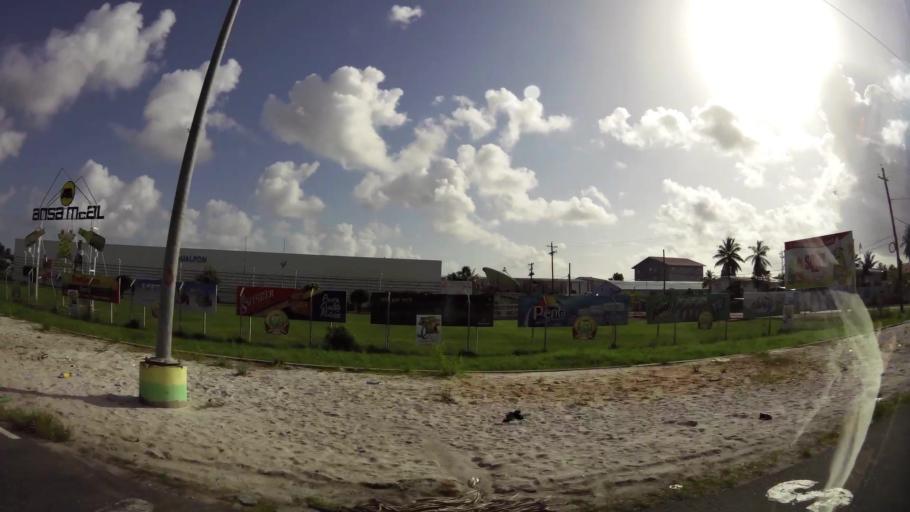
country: GY
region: Demerara-Mahaica
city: Georgetown
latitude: 6.8105
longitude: -58.0596
